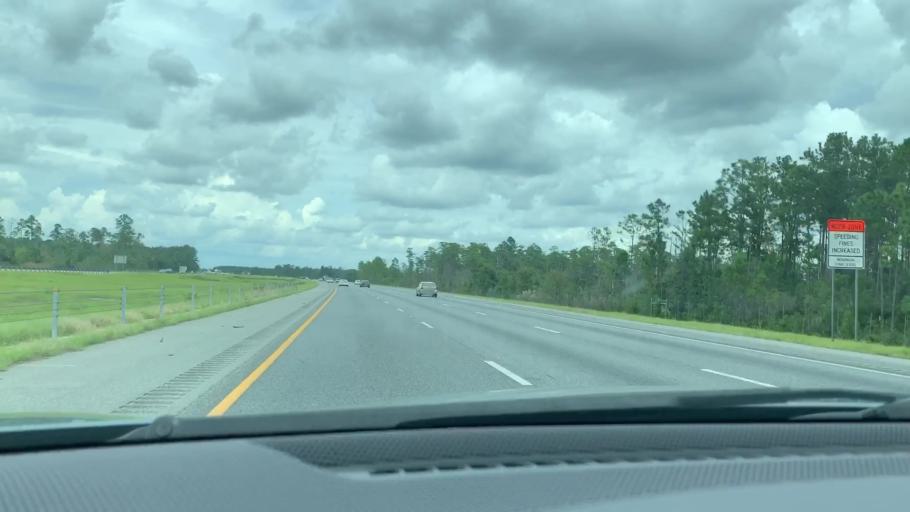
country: US
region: Georgia
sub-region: McIntosh County
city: Darien
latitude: 31.4126
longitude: -81.4440
